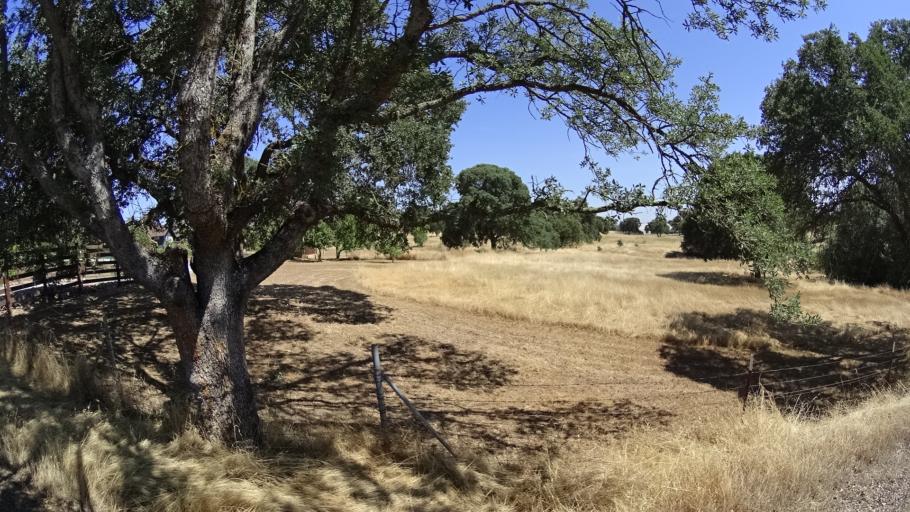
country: US
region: California
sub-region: Calaveras County
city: Rancho Calaveras
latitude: 38.1485
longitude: -120.9503
